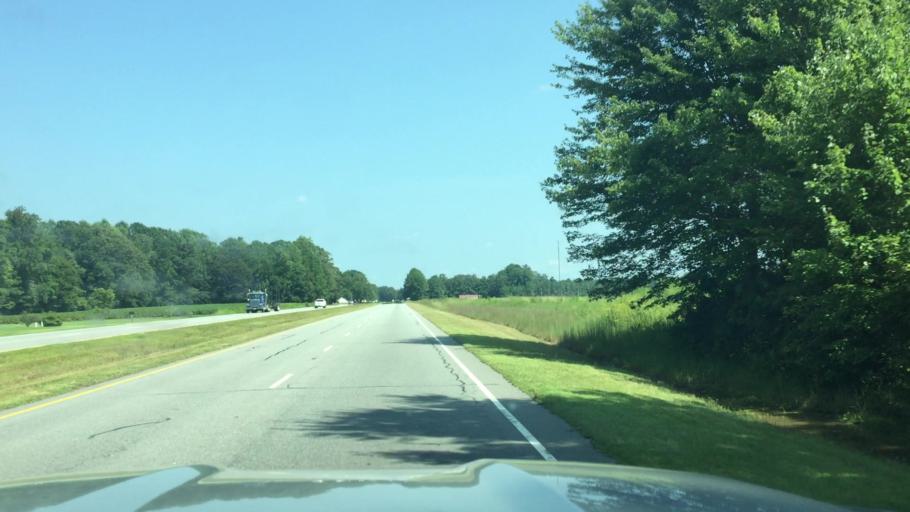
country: US
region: North Carolina
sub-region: Martin County
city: Williamston
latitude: 35.8081
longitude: -76.9577
